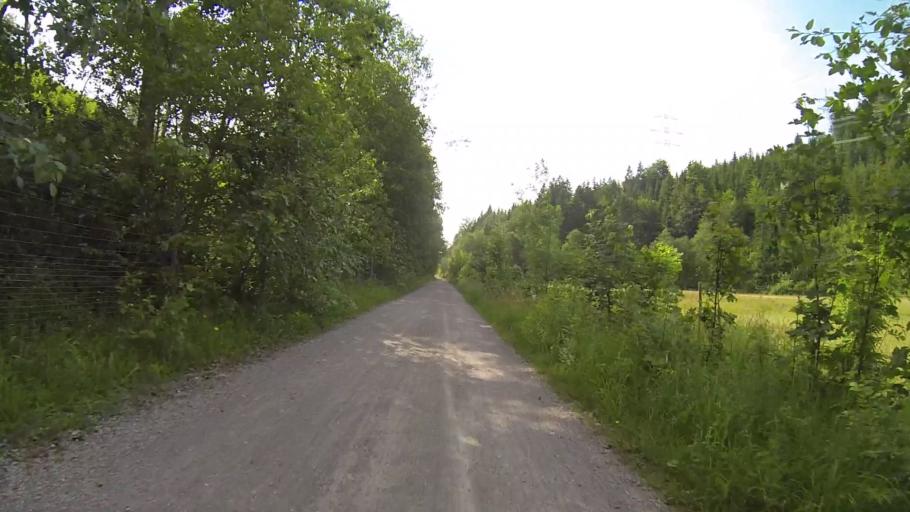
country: AT
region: Tyrol
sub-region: Politischer Bezirk Reutte
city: Pflach
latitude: 47.5207
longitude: 10.7191
